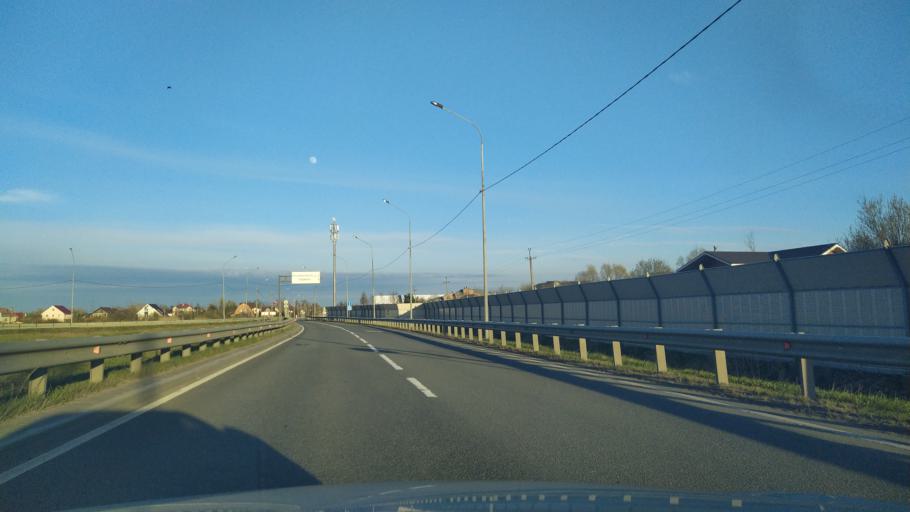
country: RU
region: St.-Petersburg
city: Aleksandrovskaya
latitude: 59.7405
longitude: 30.3203
